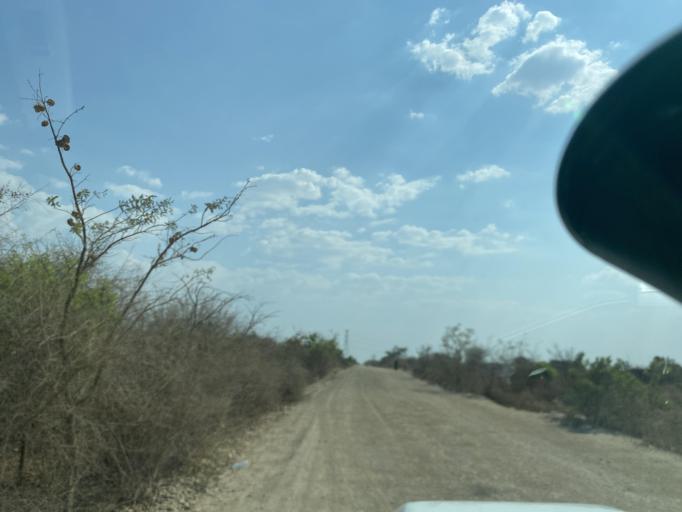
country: ZM
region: Lusaka
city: Lusaka
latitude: -15.3650
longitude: 28.0876
